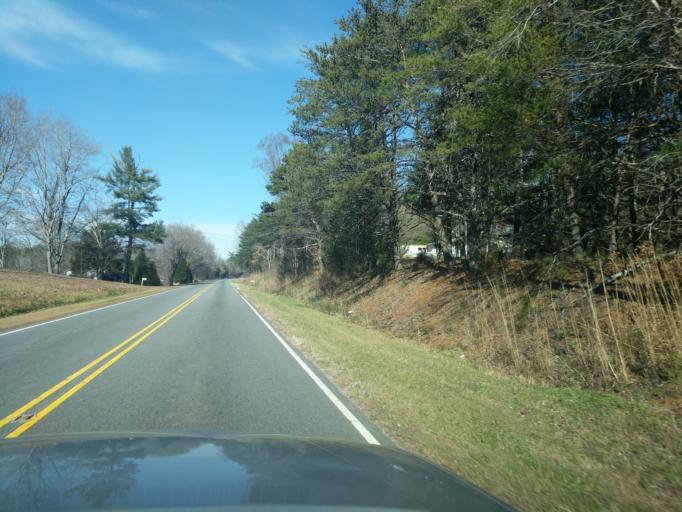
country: US
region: North Carolina
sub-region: Rutherford County
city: Rutherfordton
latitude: 35.4689
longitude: -81.9807
